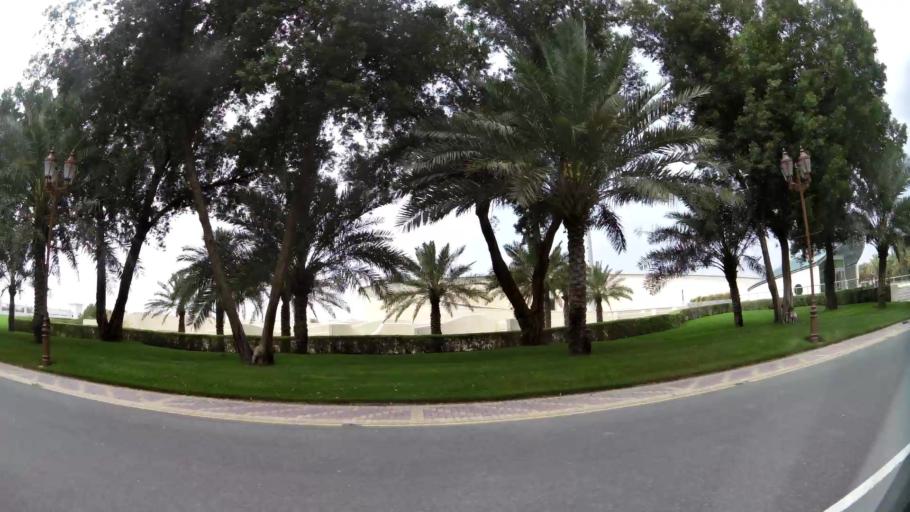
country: BH
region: Central Governorate
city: Dar Kulayb
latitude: 26.0711
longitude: 50.5278
